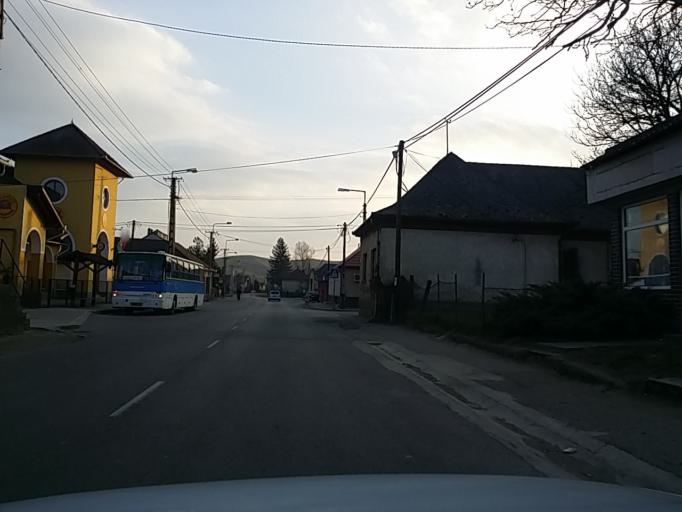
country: HU
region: Heves
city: Tarnalelesz
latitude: 48.0584
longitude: 20.1839
